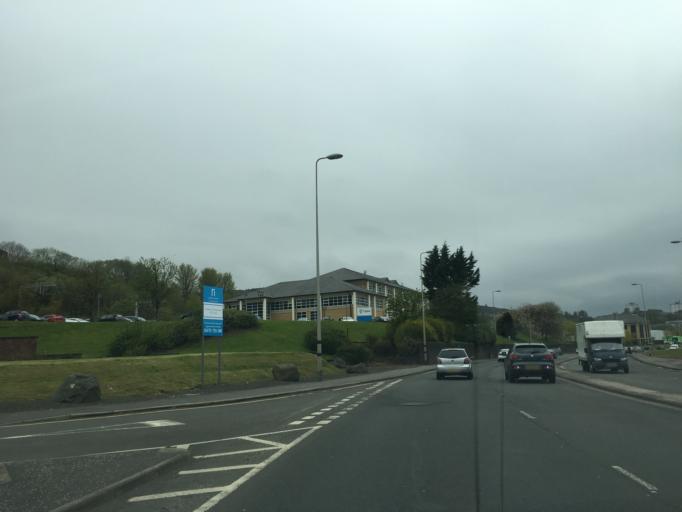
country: GB
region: Scotland
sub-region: Inverclyde
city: Greenock
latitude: 55.9437
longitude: -4.7382
